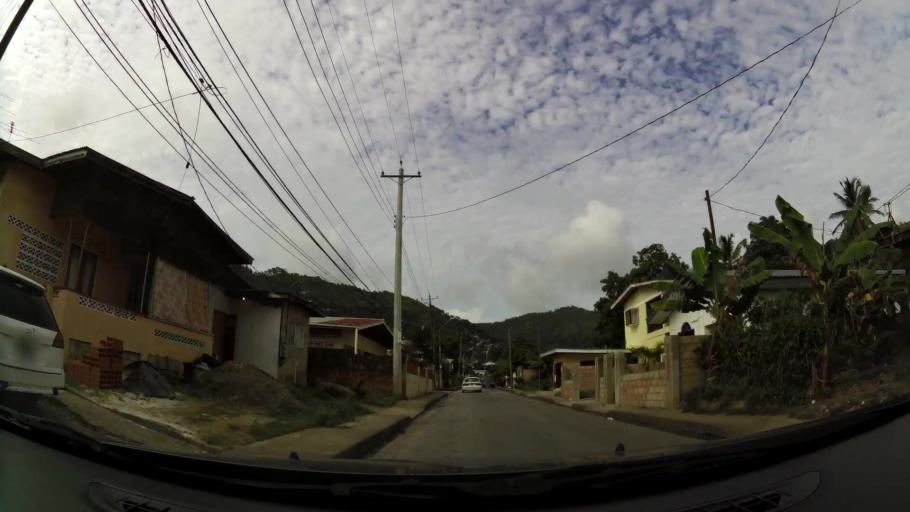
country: TT
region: City of Port of Spain
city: Mucurapo
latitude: 10.6862
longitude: -61.5941
